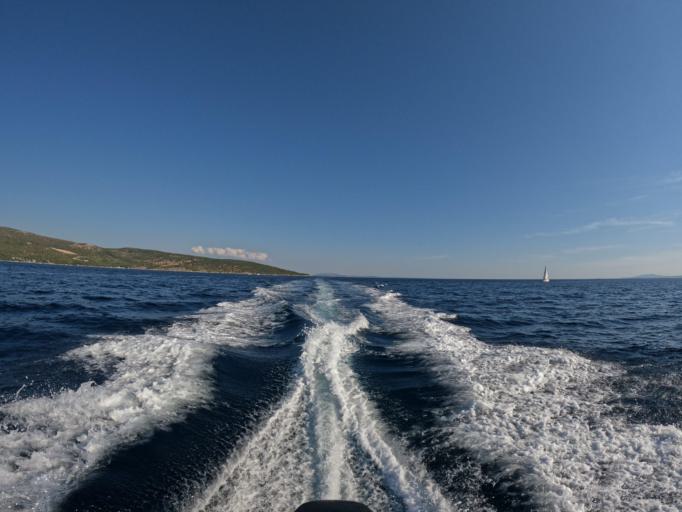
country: HR
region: Primorsko-Goranska
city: Punat
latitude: 44.9966
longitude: 14.6011
